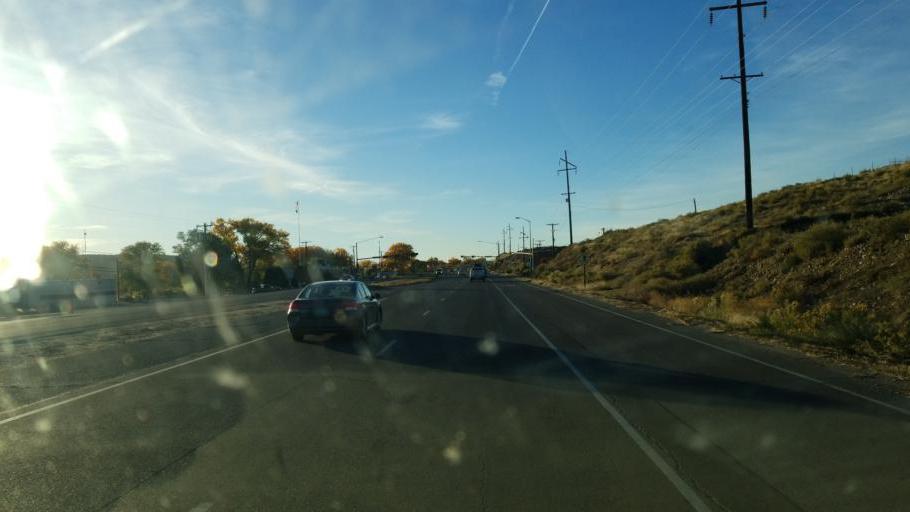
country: US
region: New Mexico
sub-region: San Juan County
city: Farmington
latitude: 36.7095
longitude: -108.1335
